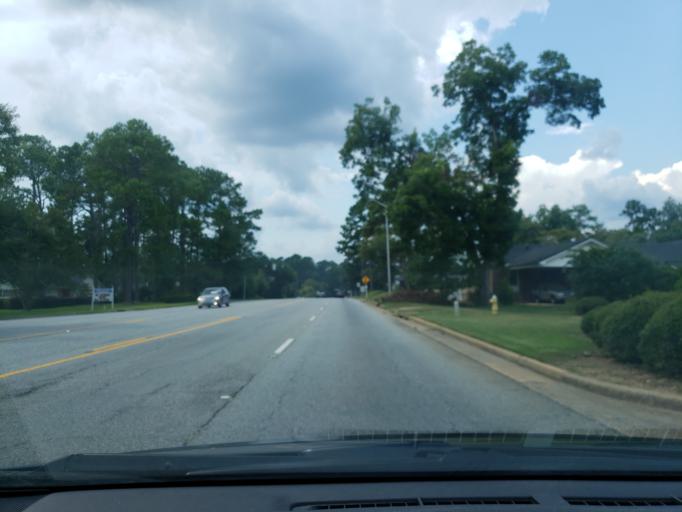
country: US
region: Georgia
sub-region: Dougherty County
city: Albany
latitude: 31.5893
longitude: -84.1882
